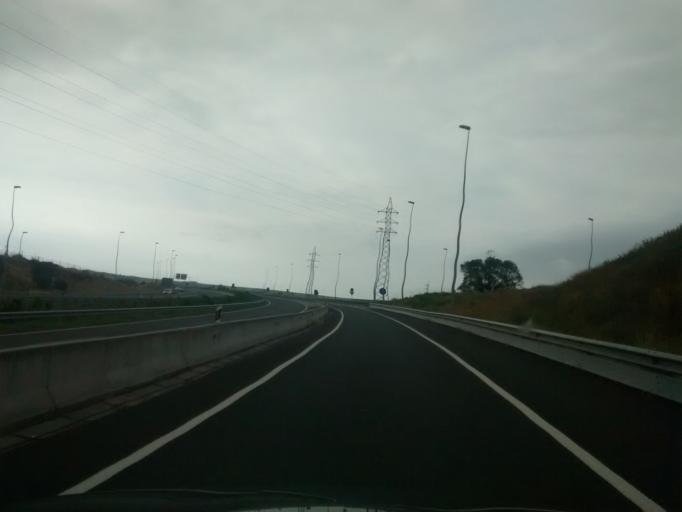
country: ES
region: Cantabria
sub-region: Provincia de Cantabria
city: Santa Cruz de Bezana
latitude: 43.4435
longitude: -3.8766
